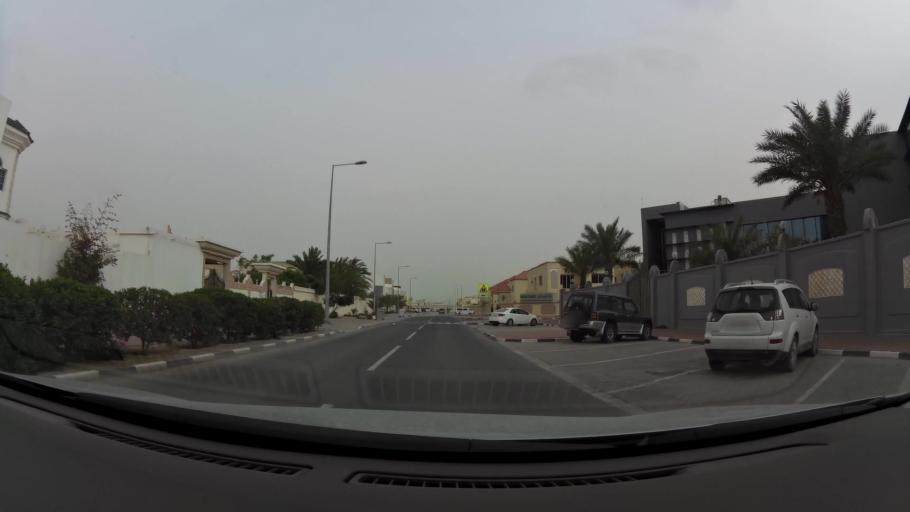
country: QA
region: Baladiyat ad Dawhah
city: Doha
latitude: 25.2450
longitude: 51.5110
